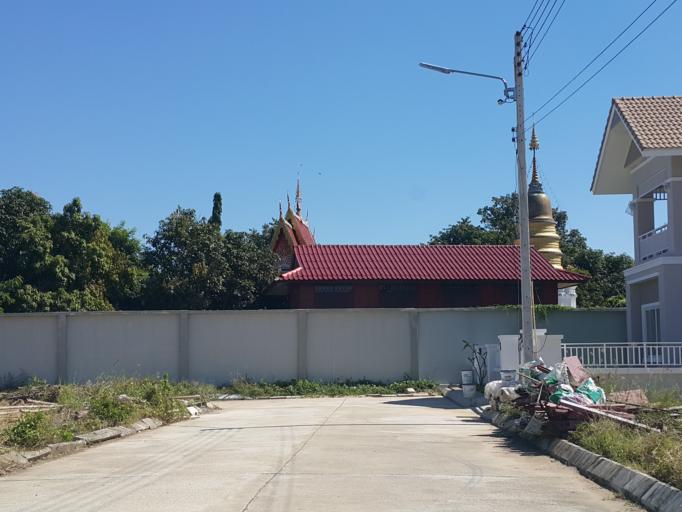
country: TH
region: Chiang Mai
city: San Sai
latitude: 18.8098
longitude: 99.0636
